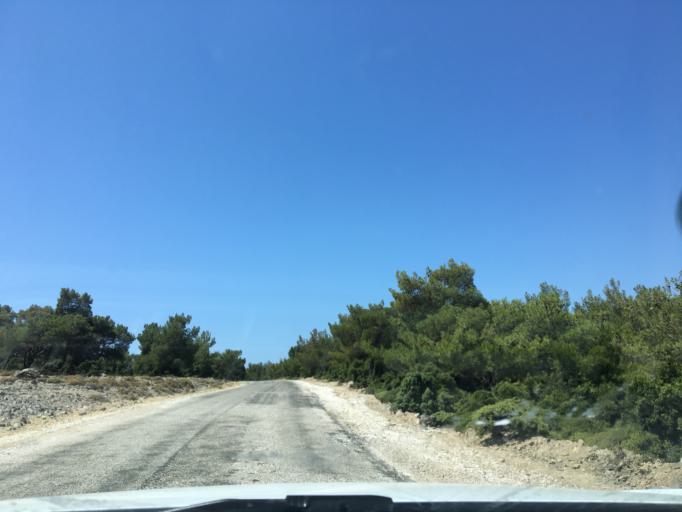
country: TR
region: Canakkale
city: Gulpinar
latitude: 39.4924
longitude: 26.1212
